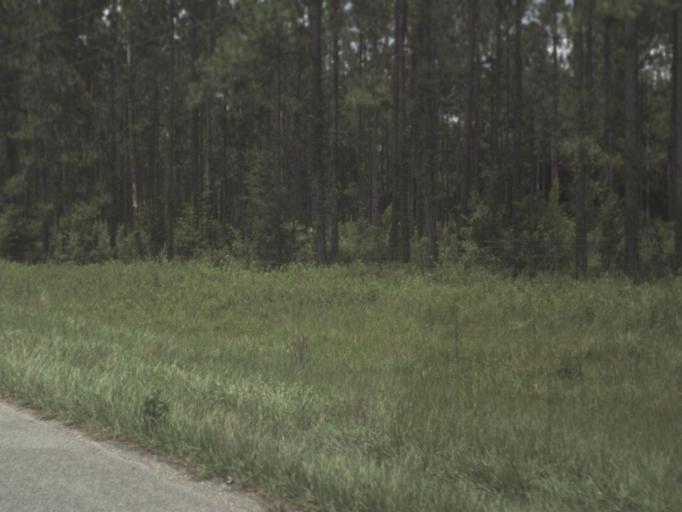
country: US
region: Florida
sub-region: Madison County
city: Madison
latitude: 30.6156
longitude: -83.4362
